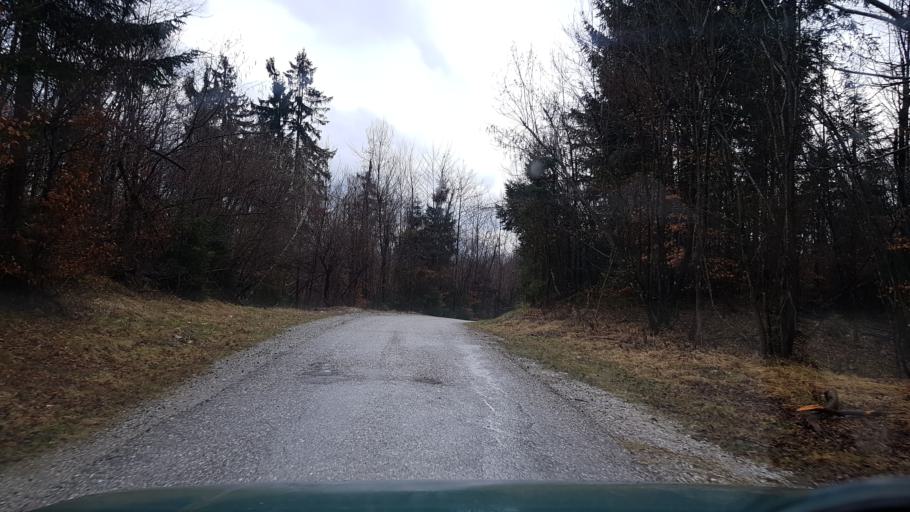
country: SI
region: Cerkno
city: Cerkno
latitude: 46.1336
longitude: 13.8740
